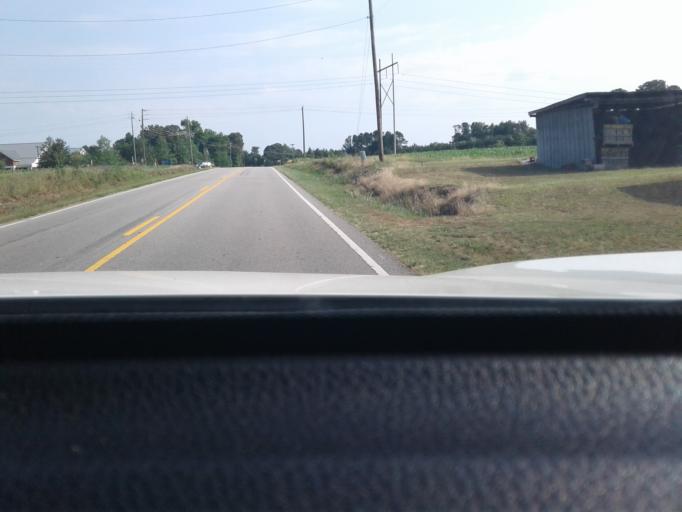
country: US
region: North Carolina
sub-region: Johnston County
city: Benson
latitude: 35.3951
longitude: -78.5431
